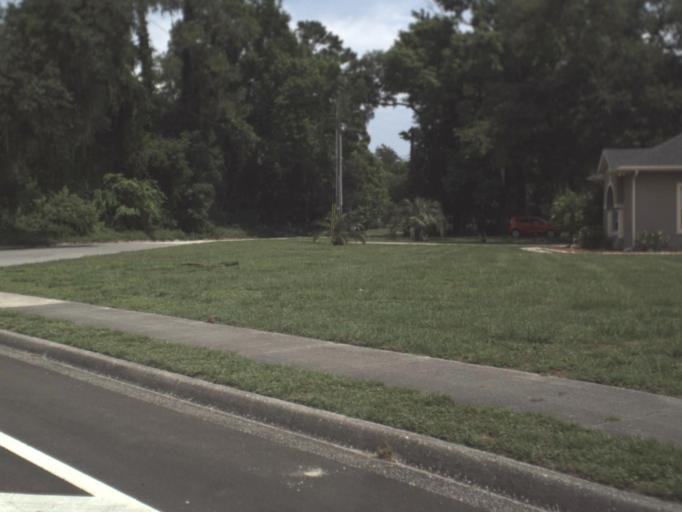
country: US
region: Florida
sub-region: Alachua County
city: Gainesville
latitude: 29.6322
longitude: -82.2665
